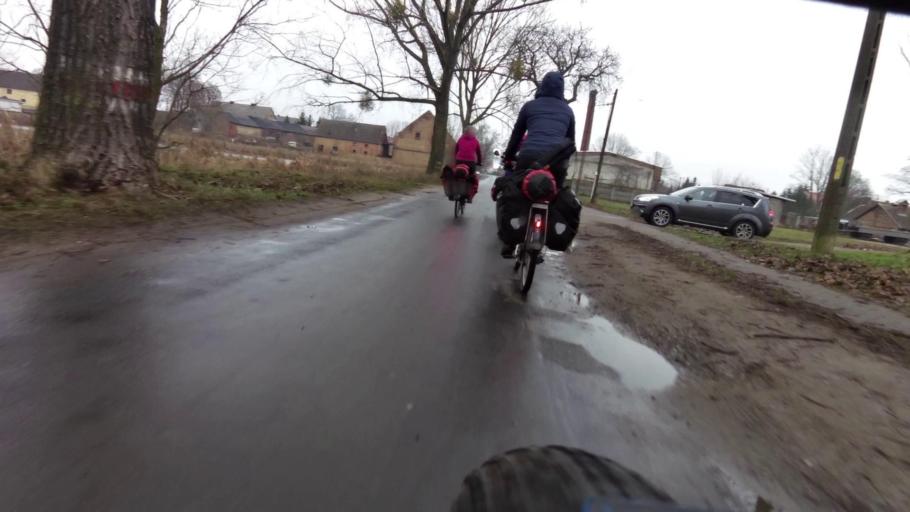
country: PL
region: West Pomeranian Voivodeship
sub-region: Powiat mysliborski
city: Debno
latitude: 52.6555
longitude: 14.7209
